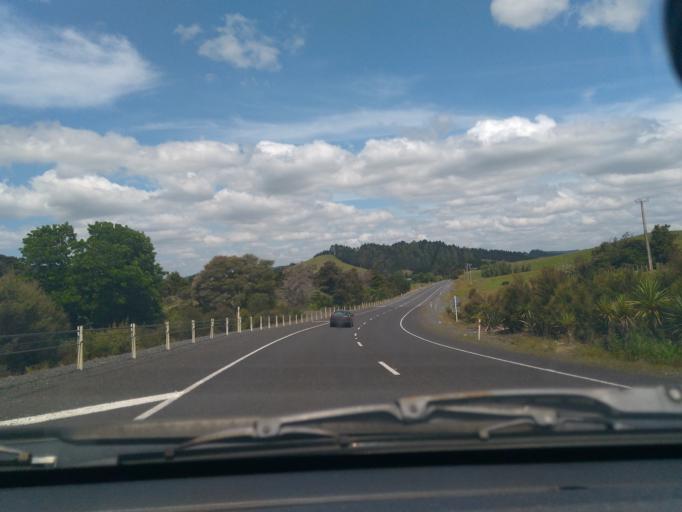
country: NZ
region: Northland
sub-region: Far North District
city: Kerikeri
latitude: -35.2764
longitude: 173.9511
